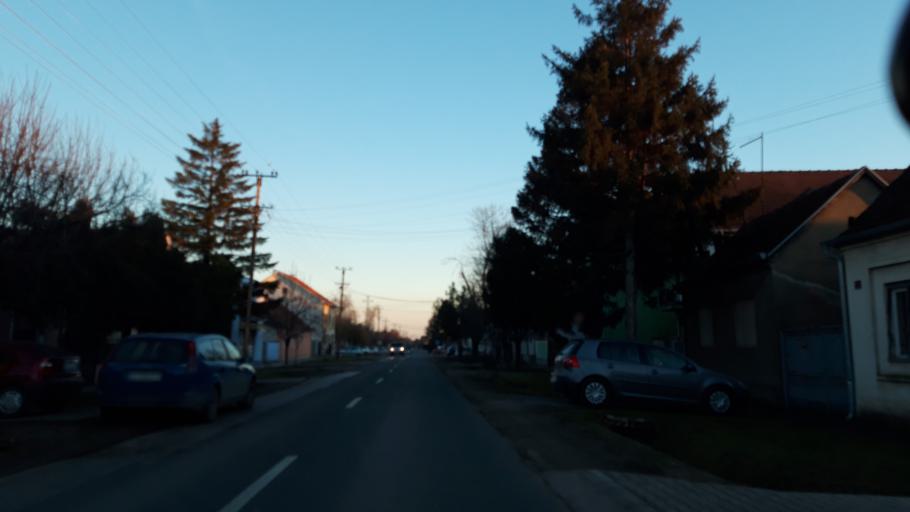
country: RS
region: Autonomna Pokrajina Vojvodina
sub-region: Sremski Okrug
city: Ingija
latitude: 45.0468
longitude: 20.0716
